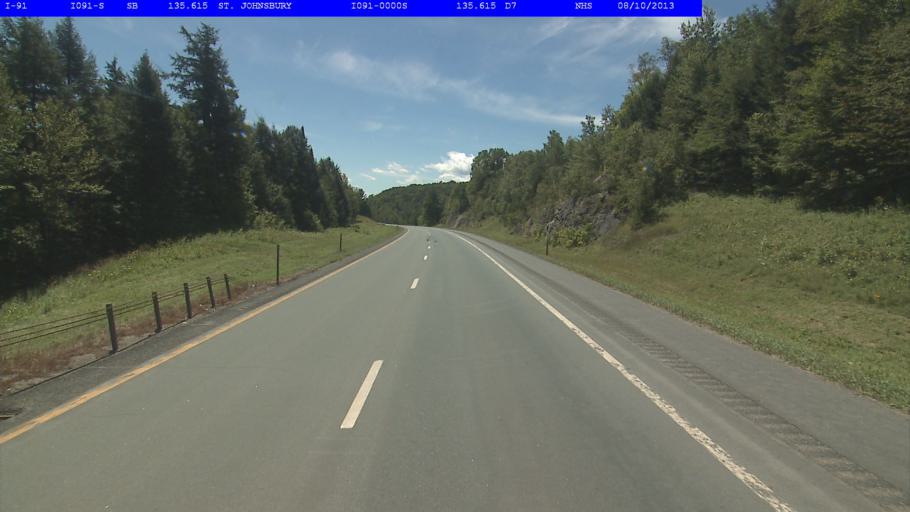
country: US
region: Vermont
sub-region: Caledonia County
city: Lyndon
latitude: 44.4983
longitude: -72.0219
